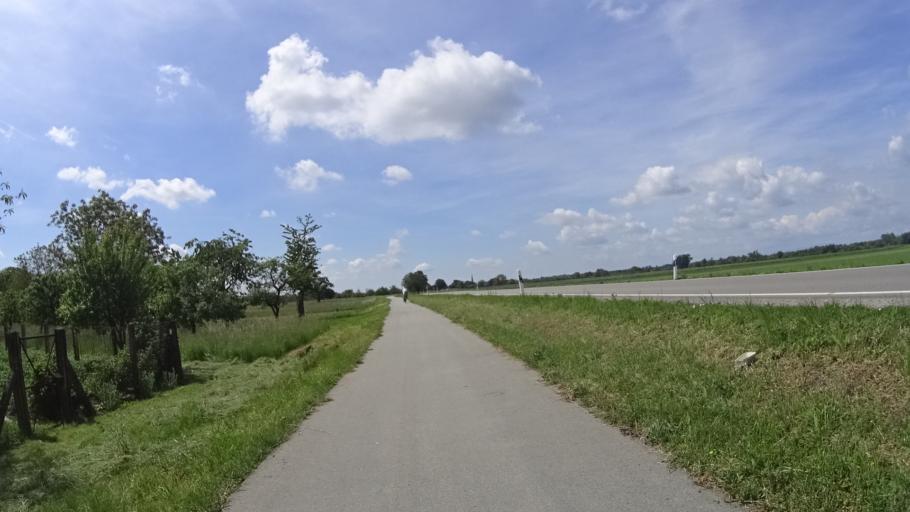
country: DE
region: Baden-Wuerttemberg
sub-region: Freiburg Region
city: Meissenheim
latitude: 48.4042
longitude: 7.7714
